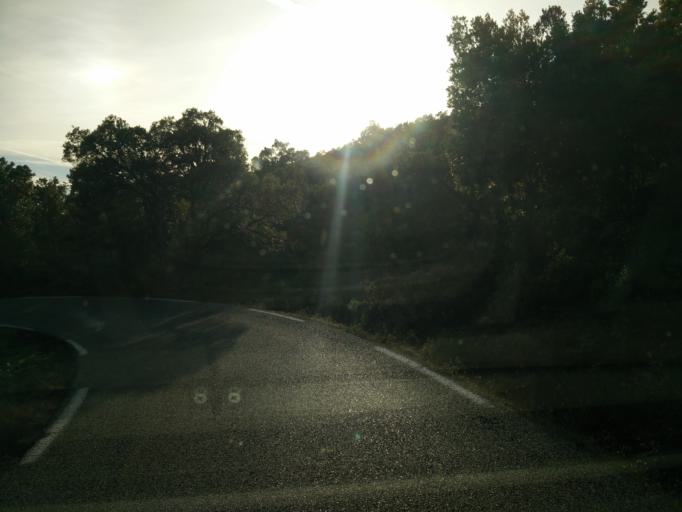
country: FR
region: Provence-Alpes-Cote d'Azur
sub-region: Departement du Var
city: Bormes-les-Mimosas
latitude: 43.1868
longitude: 6.3330
